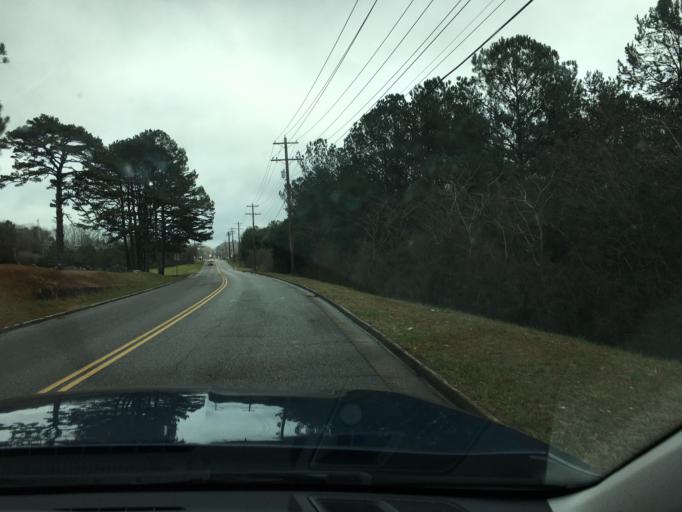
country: US
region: Tennessee
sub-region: McMinn County
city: Athens
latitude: 35.4388
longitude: -84.6281
